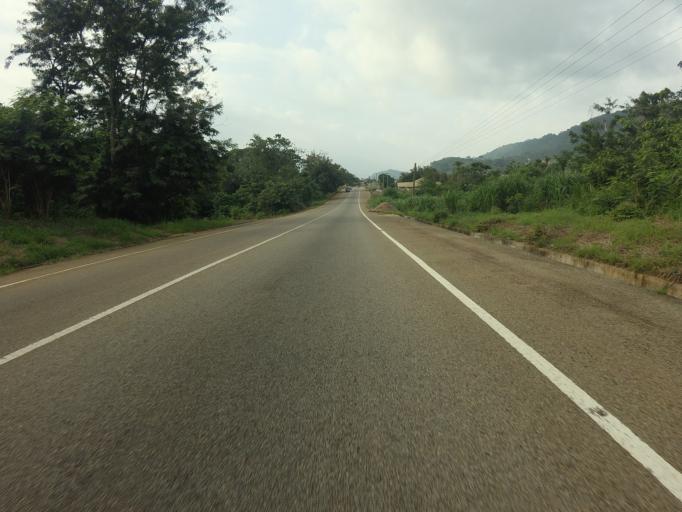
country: GH
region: Volta
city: Ho
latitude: 6.6627
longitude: 0.4727
